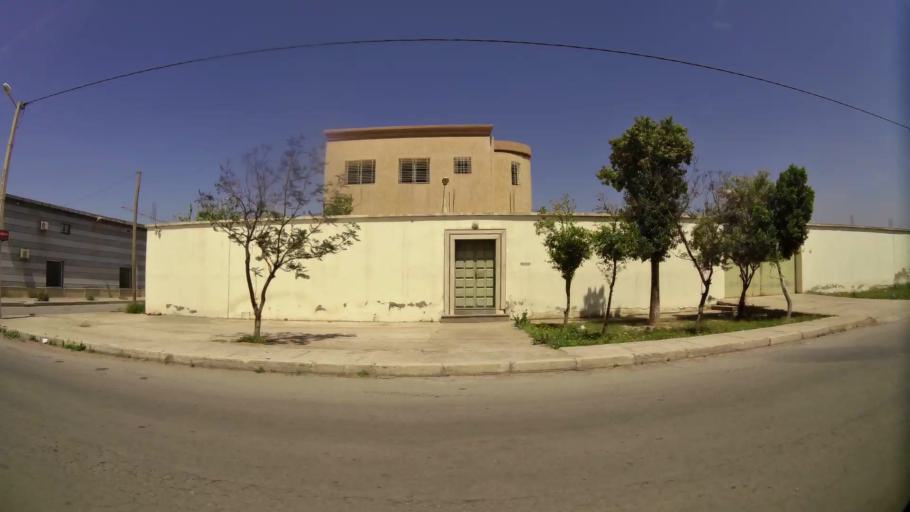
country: MA
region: Oriental
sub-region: Oujda-Angad
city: Oujda
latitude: 34.7026
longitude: -1.8863
